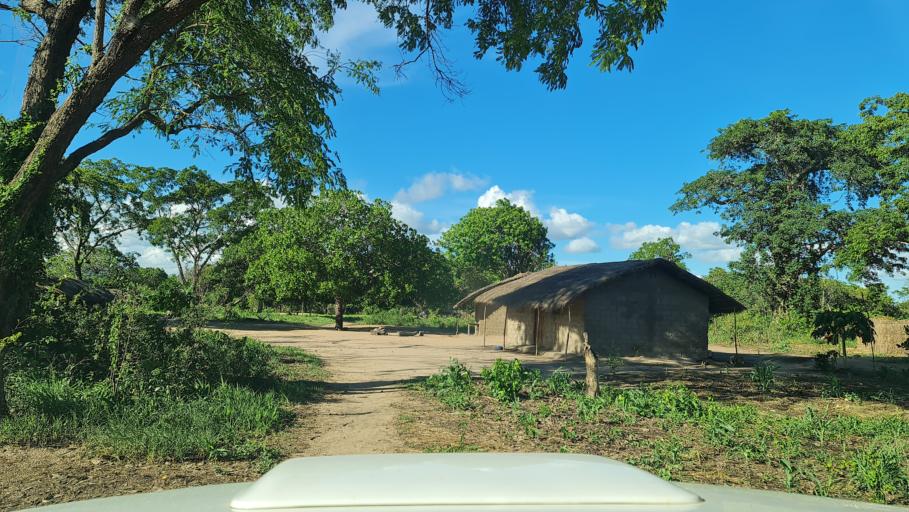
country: MZ
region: Nampula
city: Ilha de Mocambique
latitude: -15.2466
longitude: 40.1794
